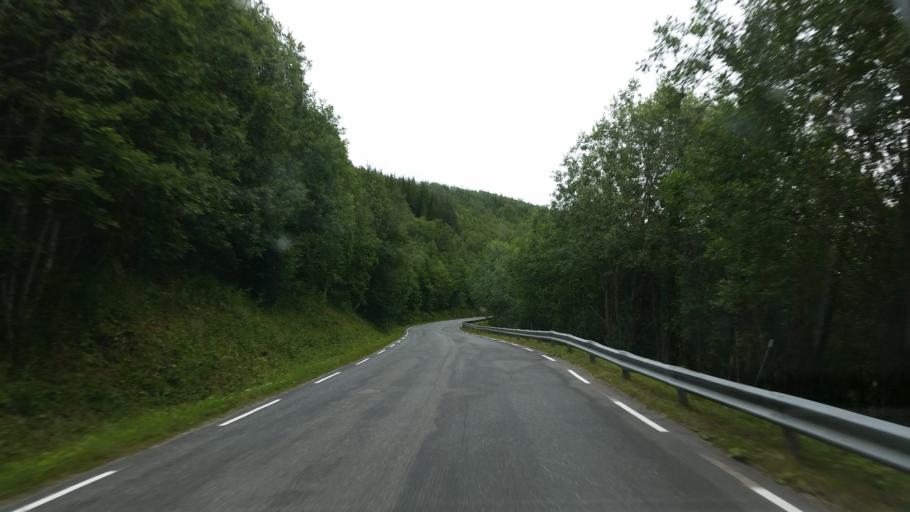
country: NO
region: Nordland
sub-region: Saltdal
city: Rognan
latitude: 67.0389
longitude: 15.0253
